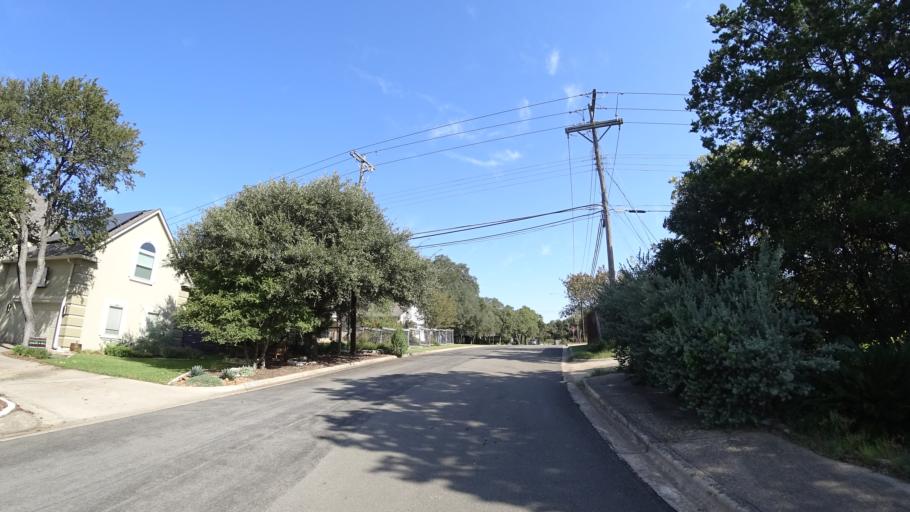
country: US
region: Texas
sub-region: Travis County
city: West Lake Hills
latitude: 30.3531
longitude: -97.7672
